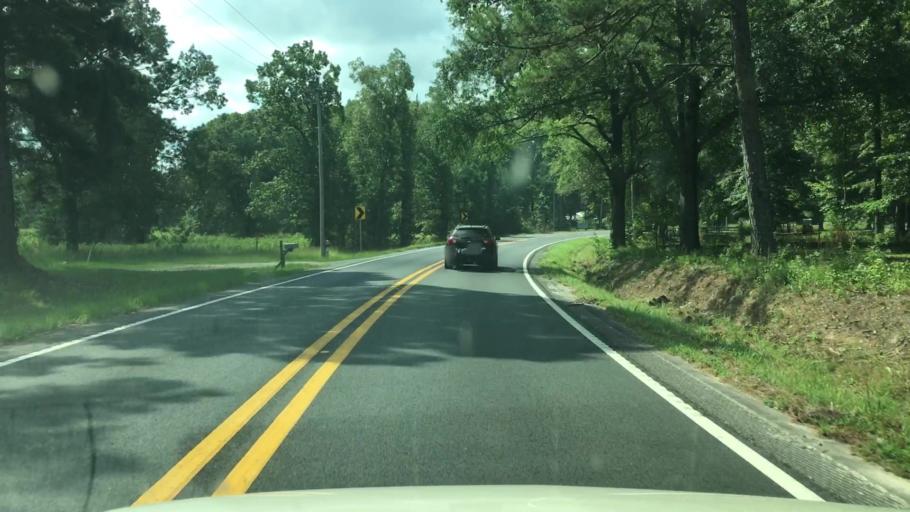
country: US
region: Arkansas
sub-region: Clark County
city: Arkadelphia
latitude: 34.2626
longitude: -93.1303
